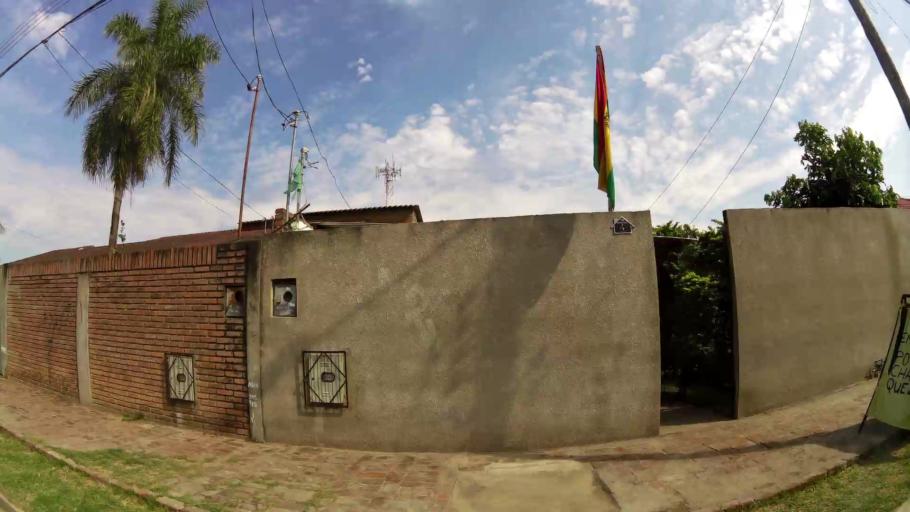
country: BO
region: Santa Cruz
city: Santa Cruz de la Sierra
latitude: -17.7283
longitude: -63.1552
